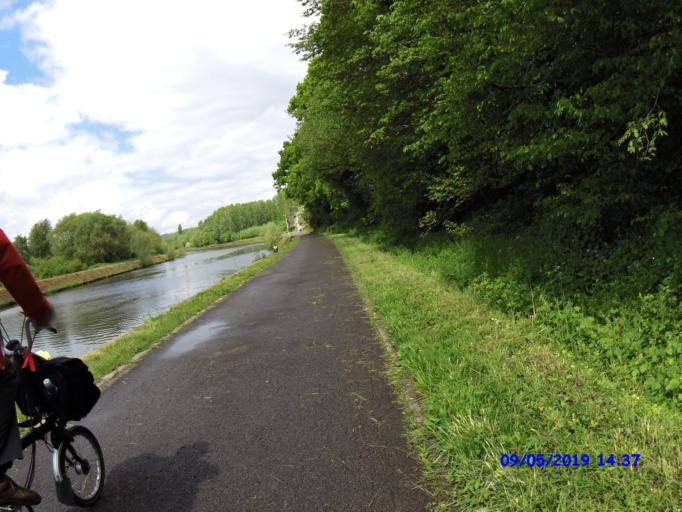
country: BE
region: Wallonia
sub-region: Province du Hainaut
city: Aiseau
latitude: 50.4389
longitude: 4.6222
